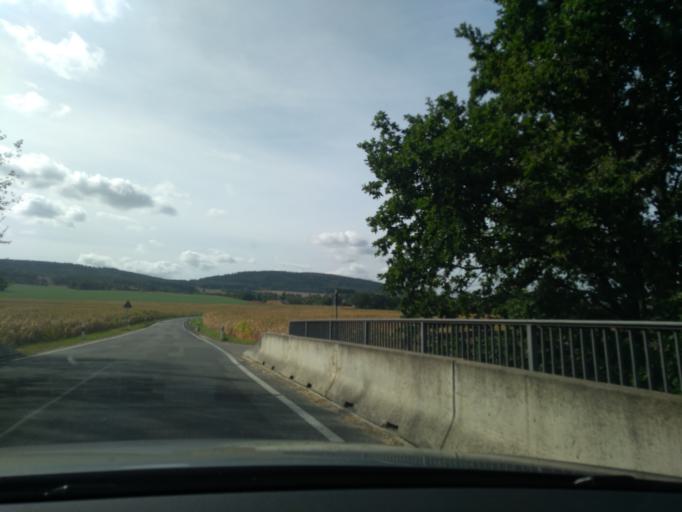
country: DE
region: Saxony
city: Kubschutz
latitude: 51.1601
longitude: 14.4653
